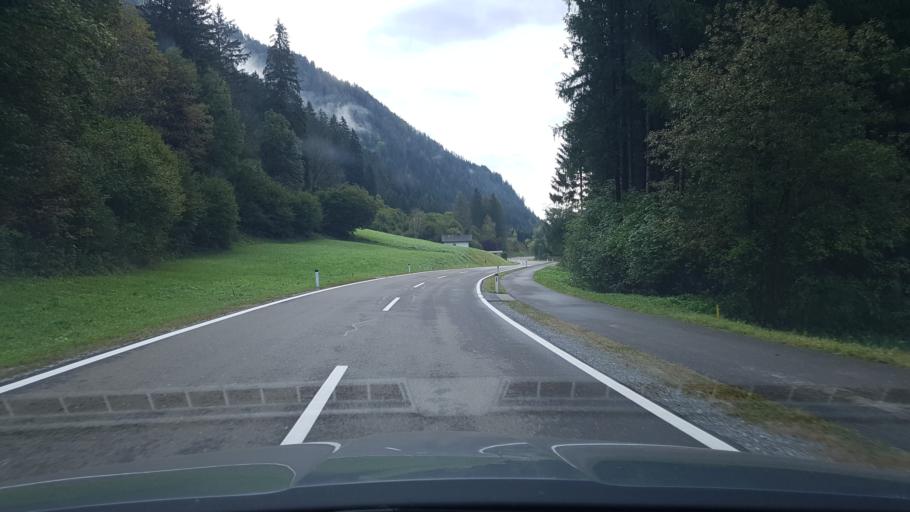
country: AT
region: Styria
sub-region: Politischer Bezirk Murau
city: Winklern bei Oberwolz
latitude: 47.1628
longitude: 14.2477
